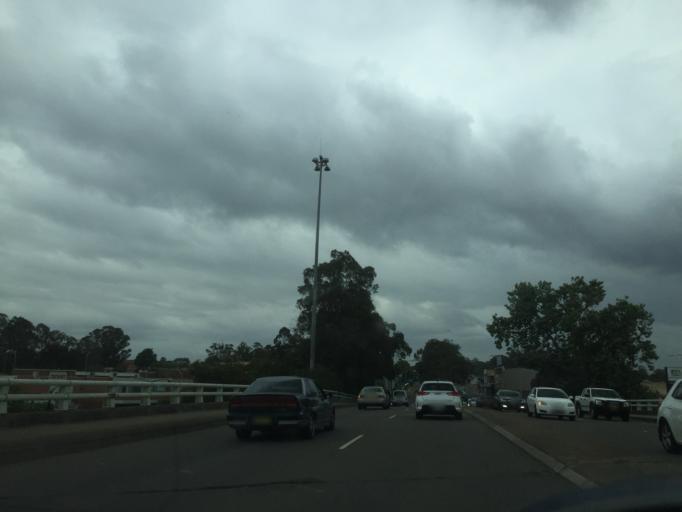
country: AU
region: New South Wales
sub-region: Blacktown
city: Blacktown
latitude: -33.7742
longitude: 150.9353
